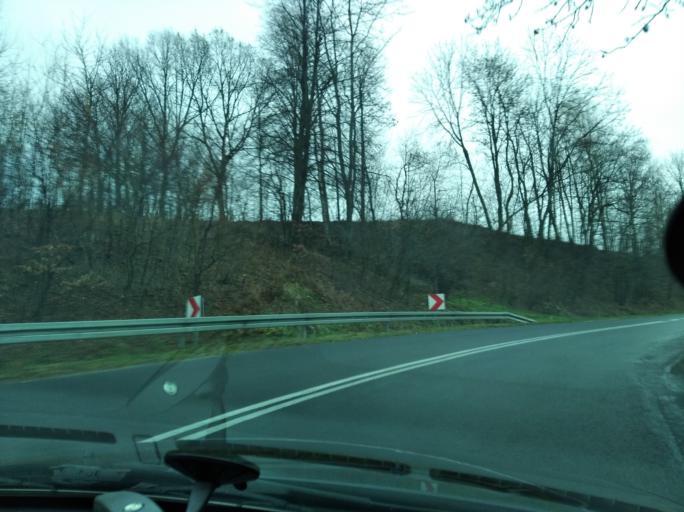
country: PL
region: Subcarpathian Voivodeship
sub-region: Powiat przeworski
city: Jawornik Polski
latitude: 49.8855
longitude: 22.2382
